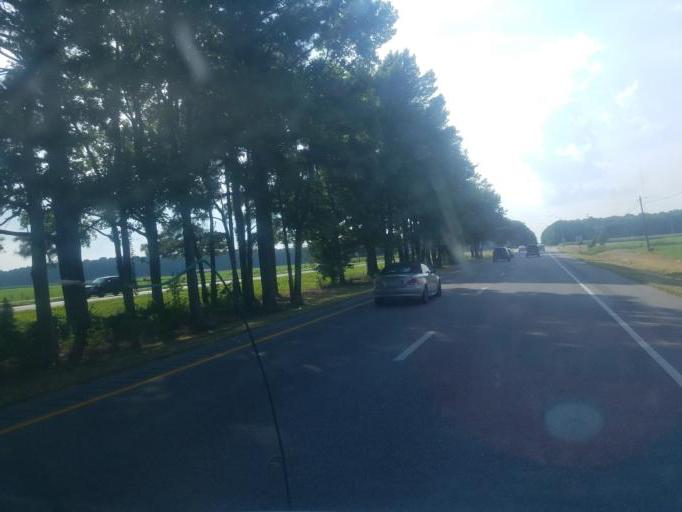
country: US
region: Maryland
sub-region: Worcester County
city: Berlin
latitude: 38.3545
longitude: -75.2432
